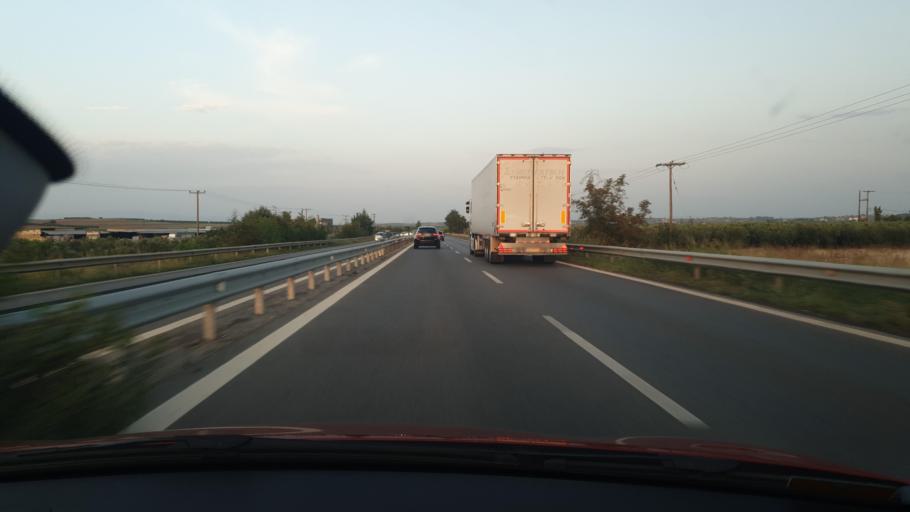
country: GR
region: Central Macedonia
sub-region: Nomos Chalkidikis
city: Nea Plagia
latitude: 40.2844
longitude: 23.1712
